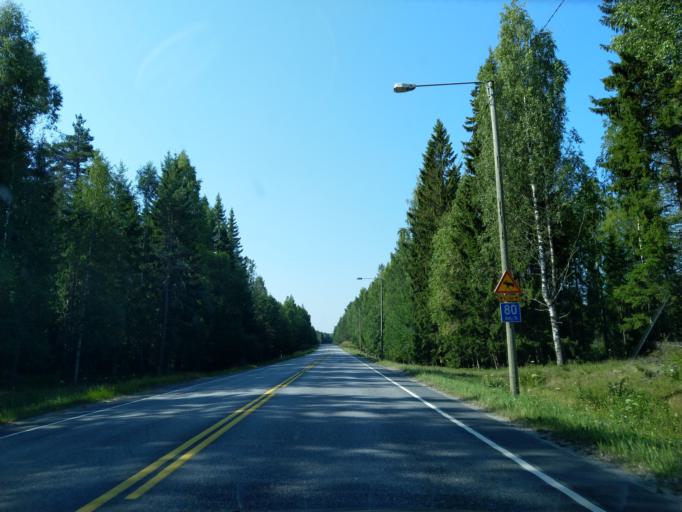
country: FI
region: Satakunta
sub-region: Pori
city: Pomarkku
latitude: 61.6488
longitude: 21.9553
